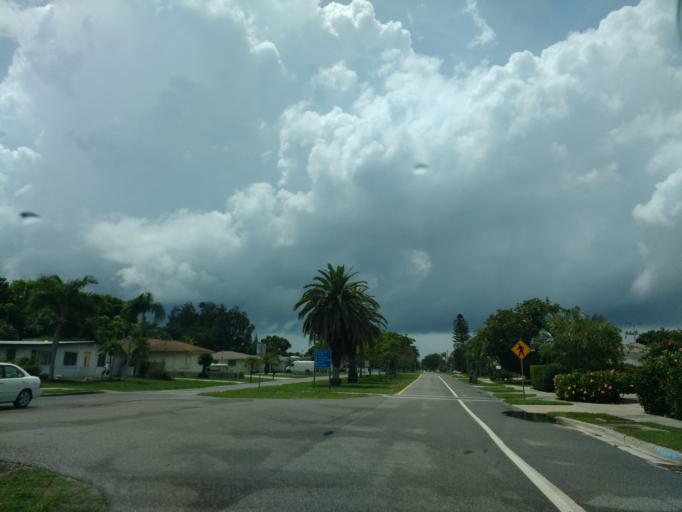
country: US
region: Florida
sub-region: Sarasota County
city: Venice
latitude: 27.0891
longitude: -82.4502
